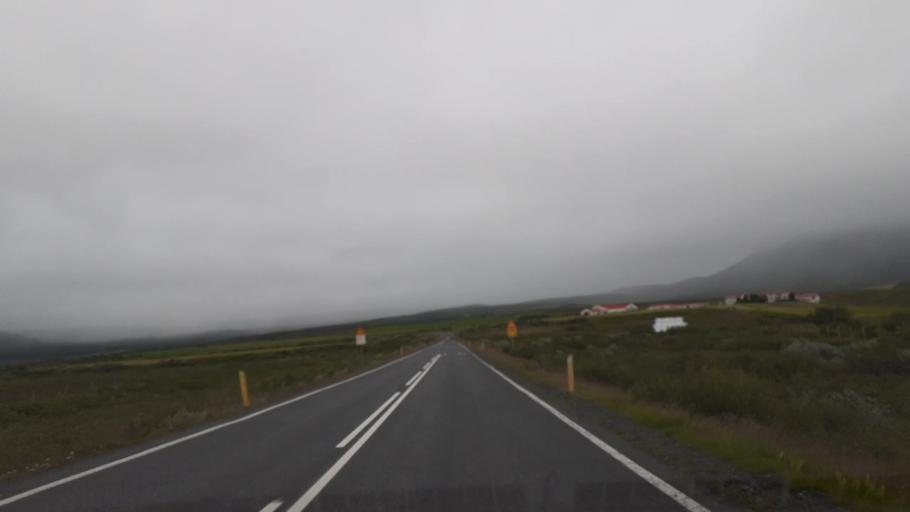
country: IS
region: Northeast
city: Husavik
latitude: 66.1089
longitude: -16.4418
